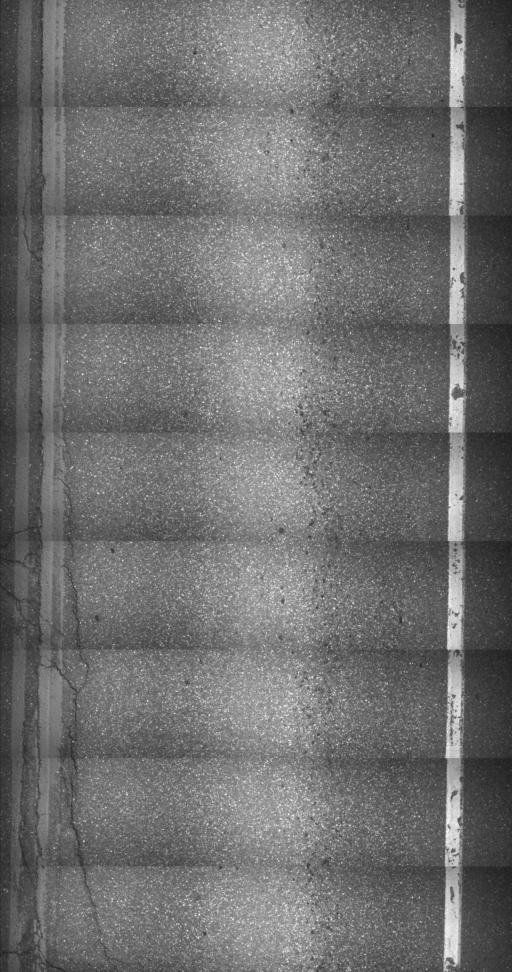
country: US
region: Vermont
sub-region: Chittenden County
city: Williston
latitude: 44.4348
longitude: -73.0393
